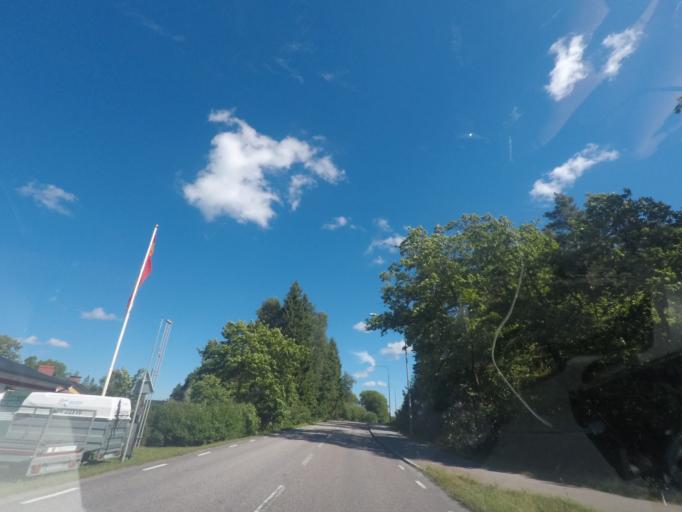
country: SE
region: Uppsala
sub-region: Knivsta Kommun
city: Knivsta
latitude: 59.8772
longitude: 17.9649
